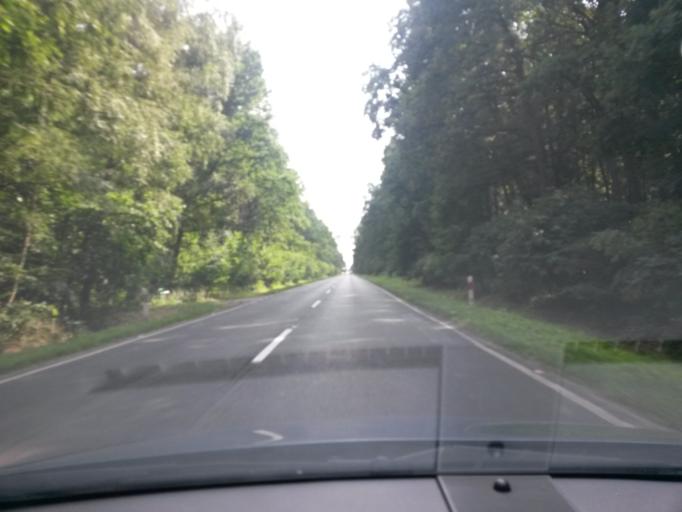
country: PL
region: Greater Poland Voivodeship
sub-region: Powiat poznanski
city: Kornik
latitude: 52.2131
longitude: 17.0708
